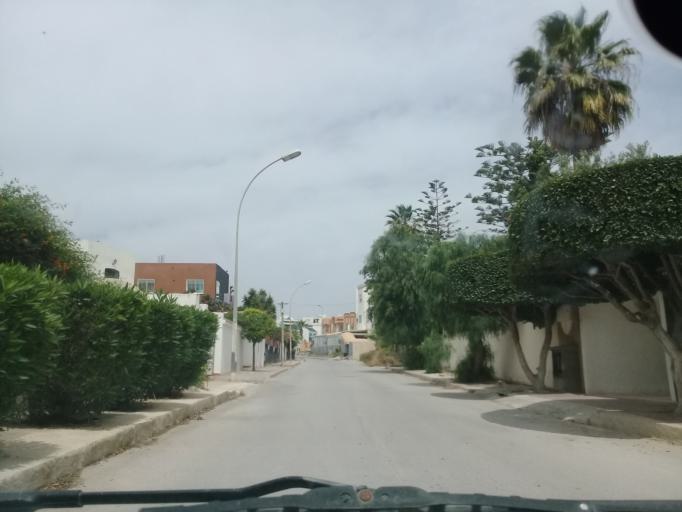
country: TN
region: Tunis
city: Tunis
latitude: 36.8412
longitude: 10.1583
